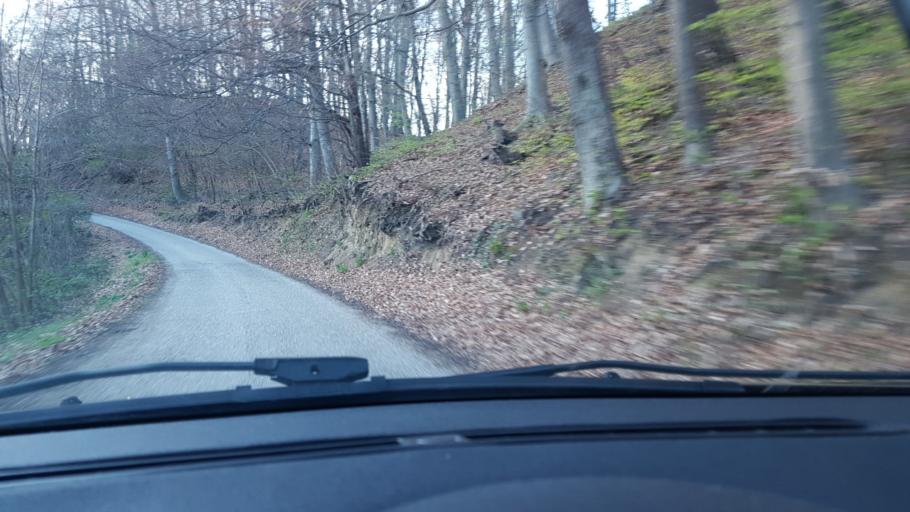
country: SI
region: Rogatec
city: Rogatec
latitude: 46.1720
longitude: 15.6882
